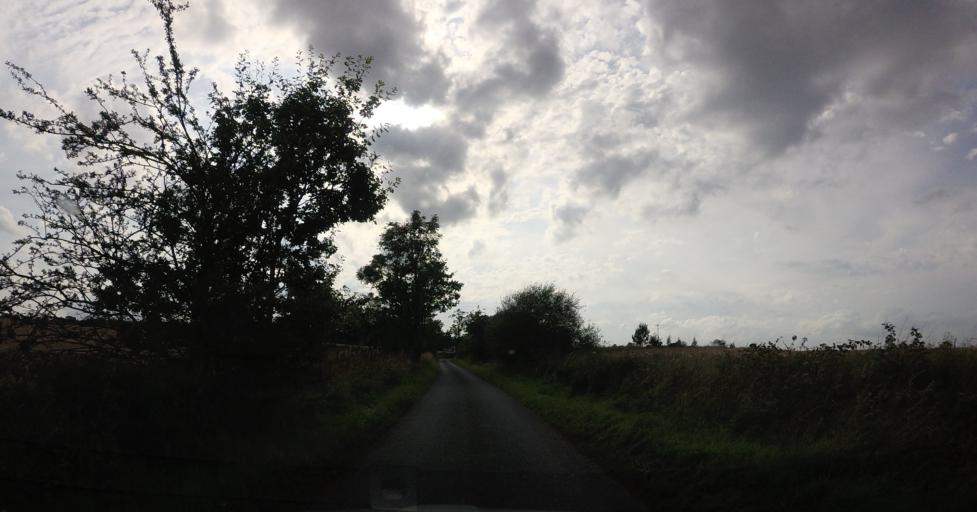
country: GB
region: Scotland
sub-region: Perth and Kinross
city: Auchterarder
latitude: 56.3007
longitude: -3.7561
